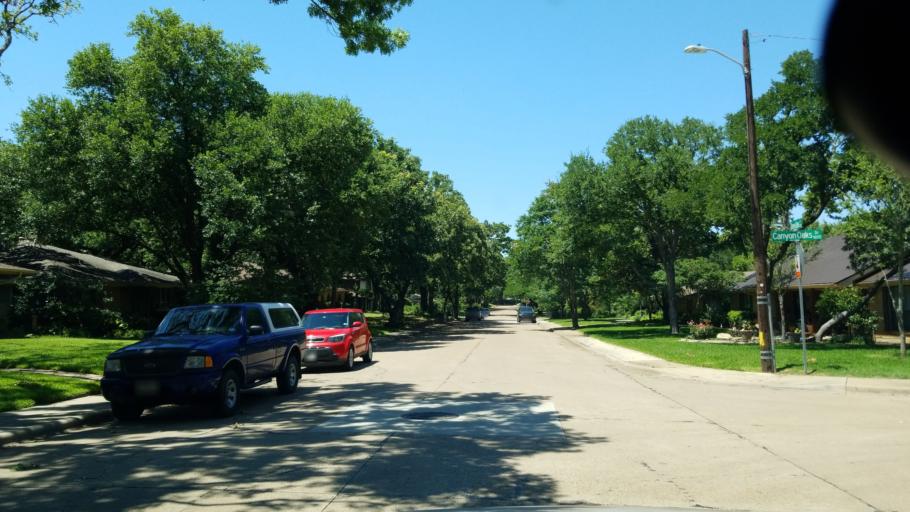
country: US
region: Texas
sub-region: Dallas County
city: Irving
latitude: 32.8317
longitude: -96.9665
